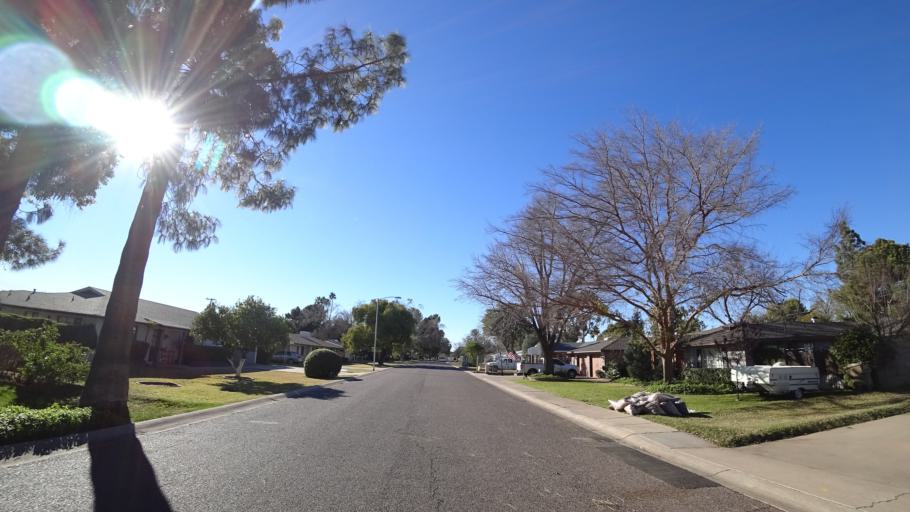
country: US
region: Arizona
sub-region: Maricopa County
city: Phoenix
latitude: 33.5180
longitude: -112.0764
